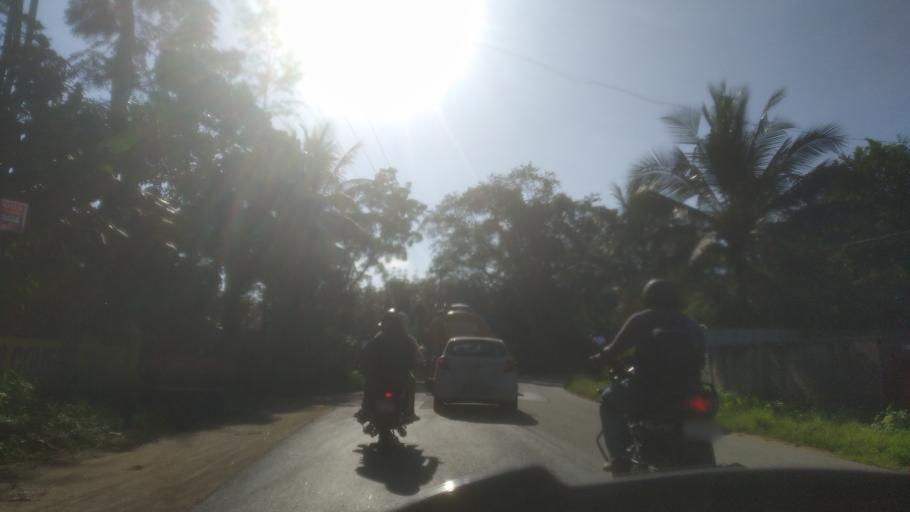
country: IN
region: Kerala
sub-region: Ernakulam
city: Ramamangalam
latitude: 9.9758
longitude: 76.5108
